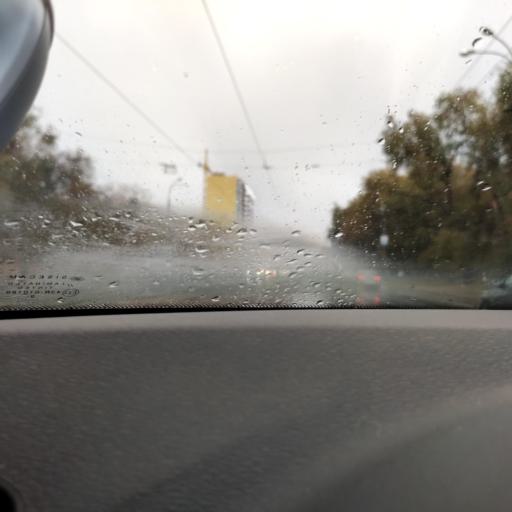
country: RU
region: Samara
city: Smyshlyayevka
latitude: 53.2042
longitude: 50.2808
